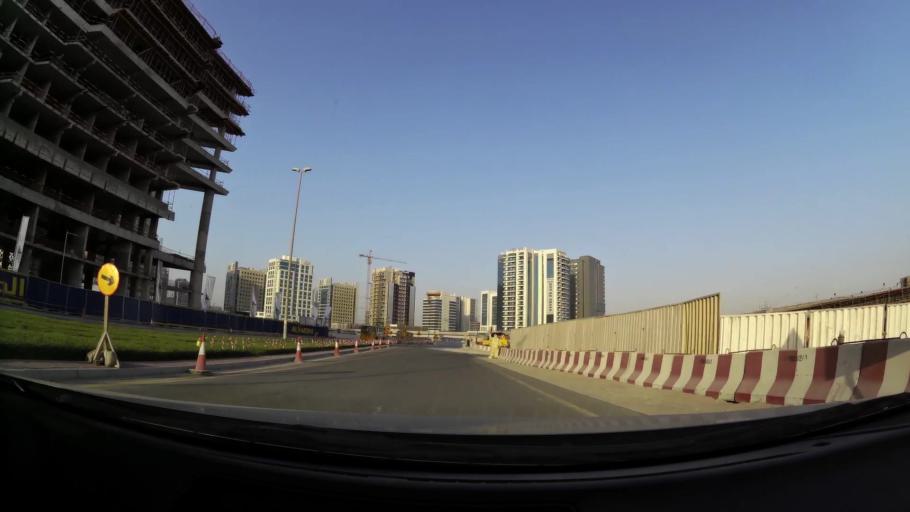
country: AE
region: Dubai
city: Dubai
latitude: 25.1775
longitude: 55.2679
